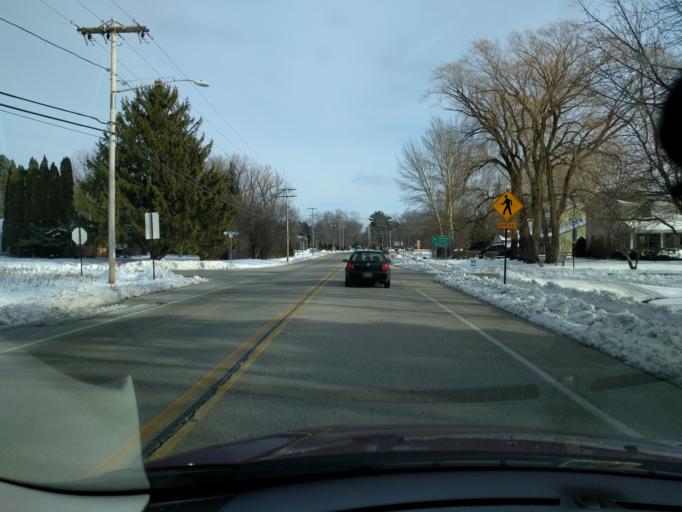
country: US
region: Wisconsin
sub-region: Milwaukee County
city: Bayside
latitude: 43.1766
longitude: -87.8983
